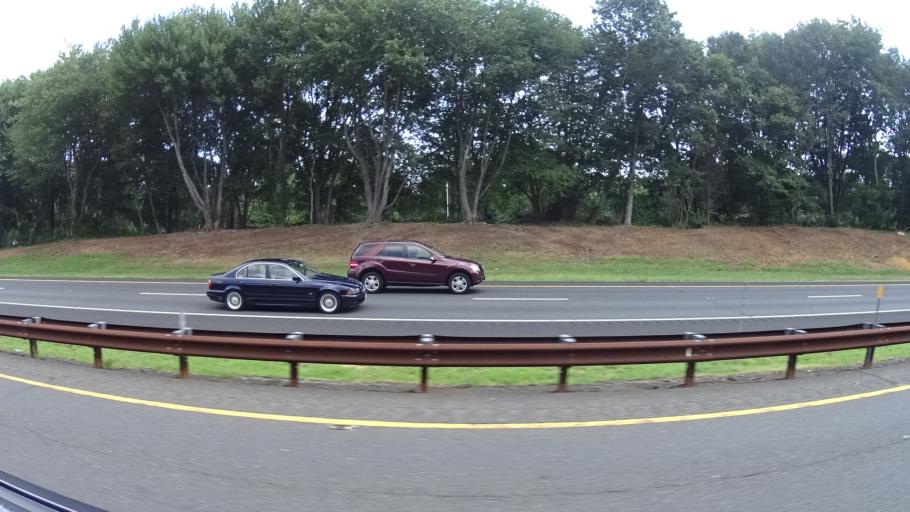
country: US
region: New Jersey
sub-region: Monmouth County
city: Lincroft
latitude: 40.3337
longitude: -74.0995
